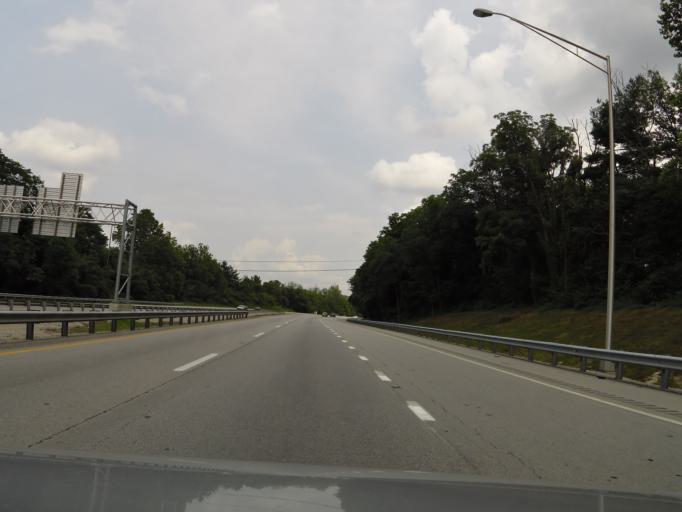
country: US
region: Kentucky
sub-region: Jefferson County
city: Northfield
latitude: 38.2913
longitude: -85.6408
